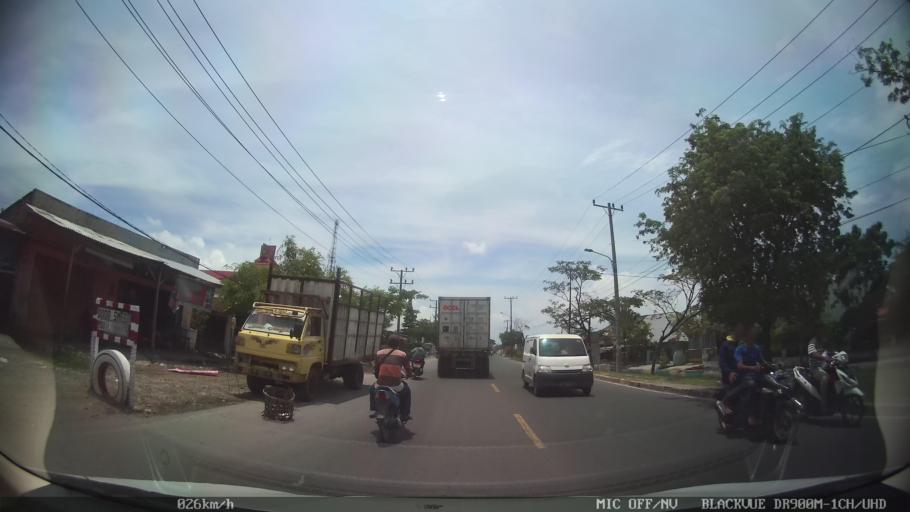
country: ID
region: North Sumatra
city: Belawan
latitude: 3.7700
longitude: 98.6821
